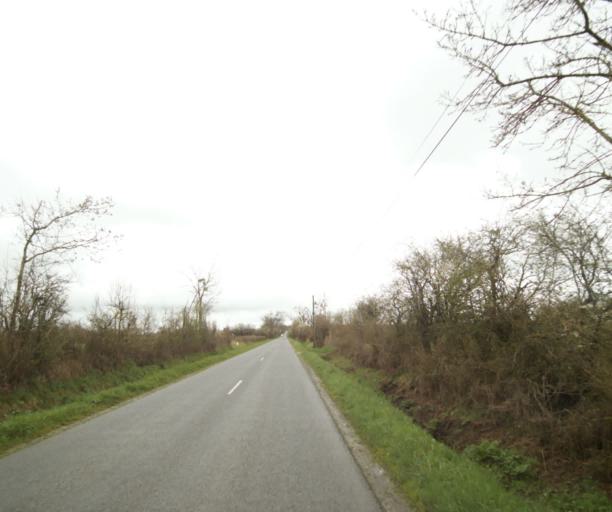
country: FR
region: Pays de la Loire
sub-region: Departement de la Loire-Atlantique
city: Bouvron
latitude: 47.4483
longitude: -1.8636
